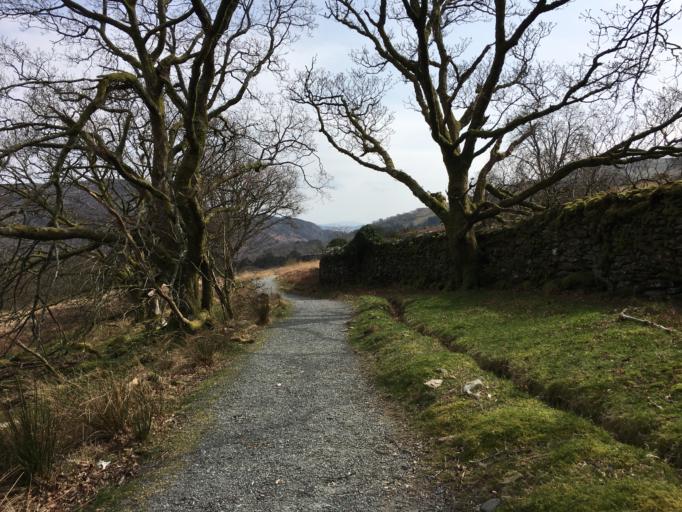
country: GB
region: Wales
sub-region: Gwynedd
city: Porthmadog
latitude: 53.0145
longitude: -4.1217
